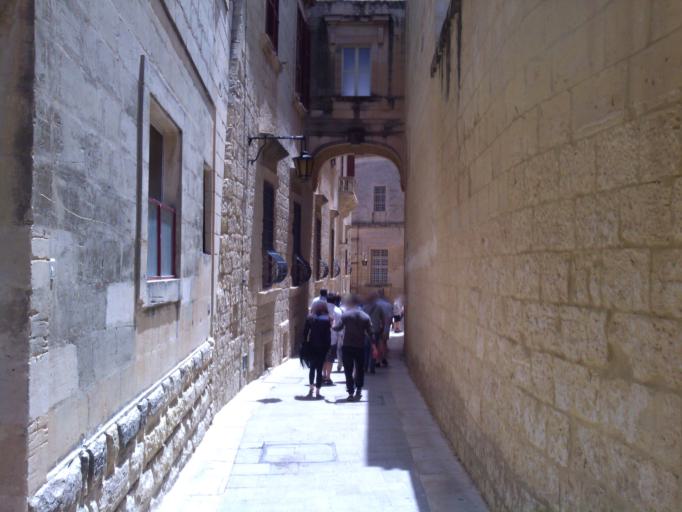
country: MT
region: L-Imdina
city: Imdina
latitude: 35.8870
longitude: 14.4038
